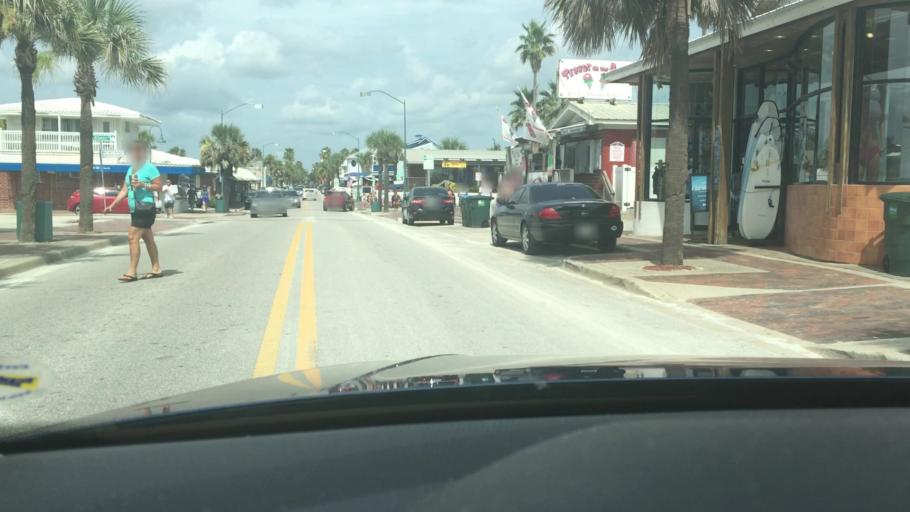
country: US
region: Florida
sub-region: Volusia County
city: New Smyrna Beach
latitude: 29.0386
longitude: -80.8962
